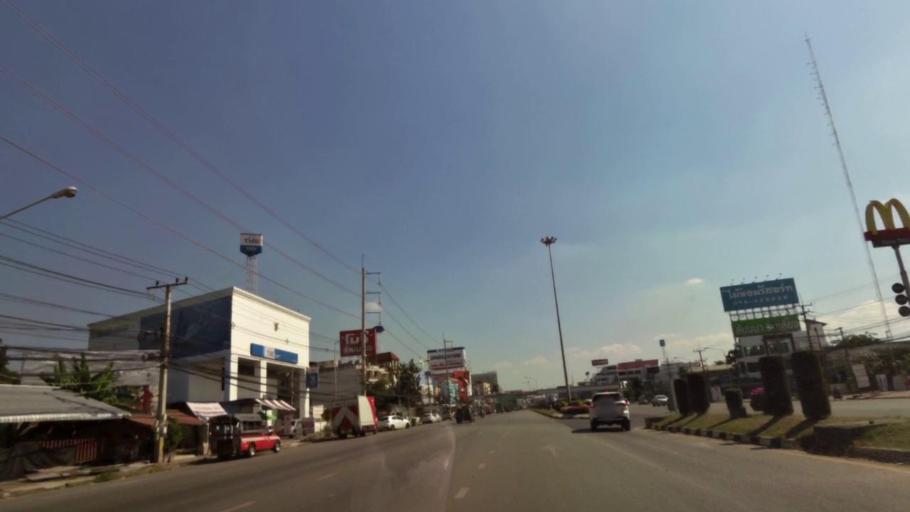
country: TH
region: Nakhon Sawan
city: Nakhon Sawan
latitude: 15.7020
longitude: 100.1166
